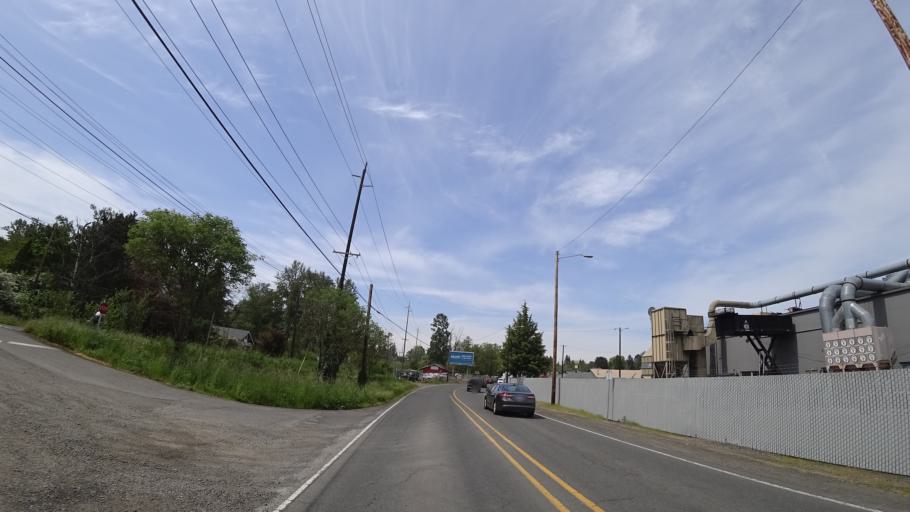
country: US
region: Oregon
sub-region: Clackamas County
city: Milwaukie
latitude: 45.4610
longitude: -122.6144
